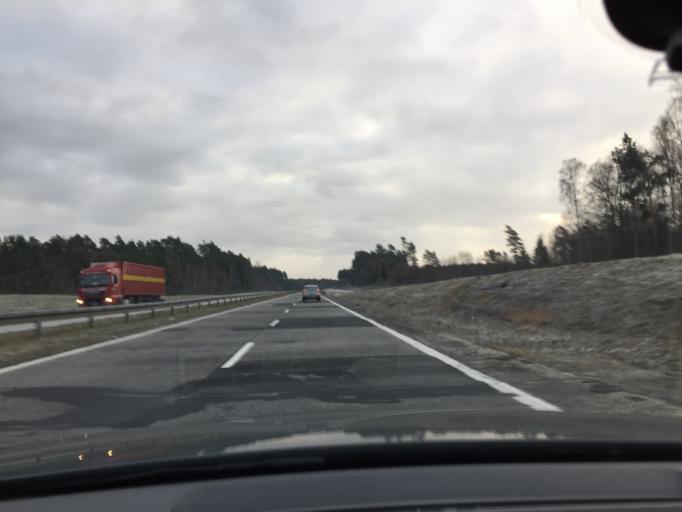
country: PL
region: Lubusz
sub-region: Powiat zarski
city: Lipinki Luzyckie
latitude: 51.5922
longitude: 15.0060
